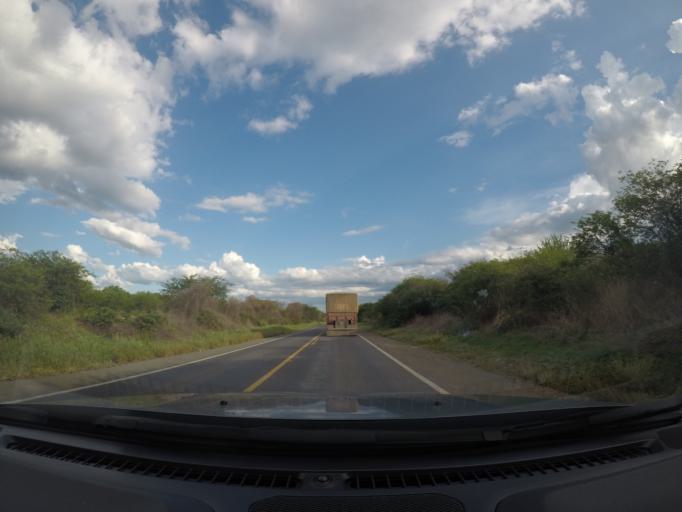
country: BR
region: Bahia
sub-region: Oliveira Dos Brejinhos
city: Beira Rio
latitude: -12.1833
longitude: -42.8315
